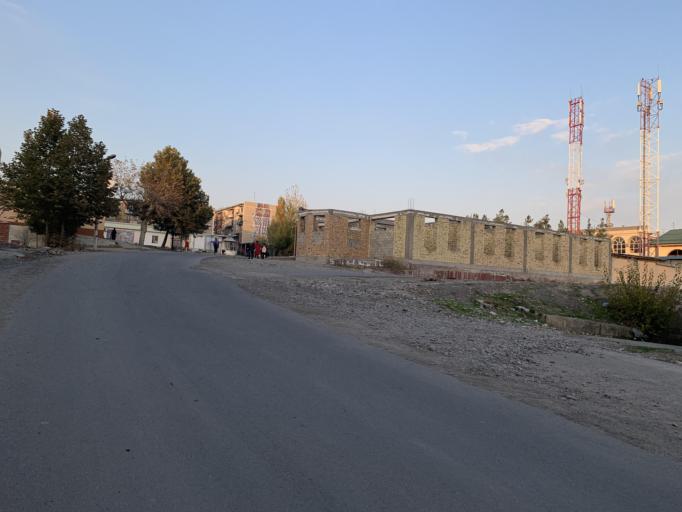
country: UZ
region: Namangan
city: Namangan Shahri
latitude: 41.0041
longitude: 71.5989
